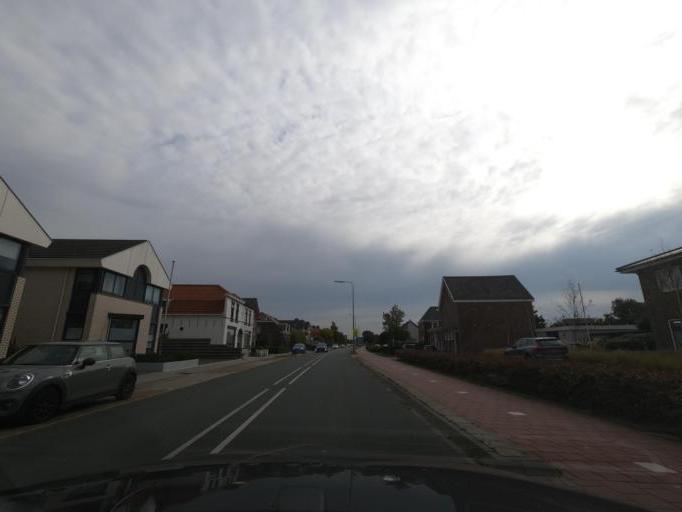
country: NL
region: South Holland
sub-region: Gemeente Westland
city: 's-Gravenzande
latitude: 52.0109
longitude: 4.1598
